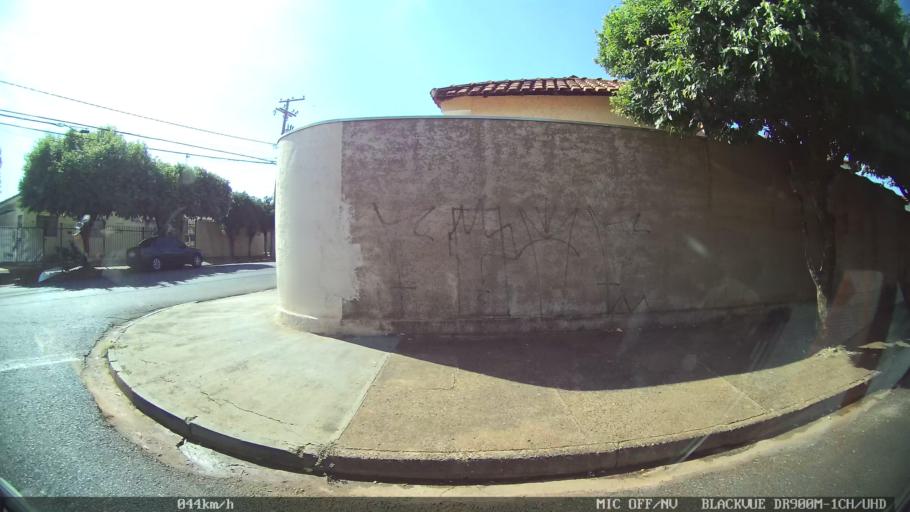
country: BR
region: Sao Paulo
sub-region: Sao Jose Do Rio Preto
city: Sao Jose do Rio Preto
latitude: -20.7859
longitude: -49.4116
